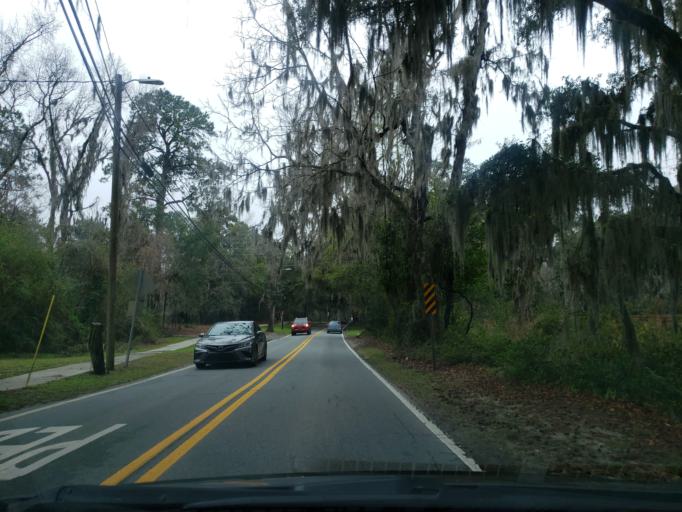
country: US
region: Georgia
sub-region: Chatham County
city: Montgomery
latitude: 31.9535
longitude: -81.1454
